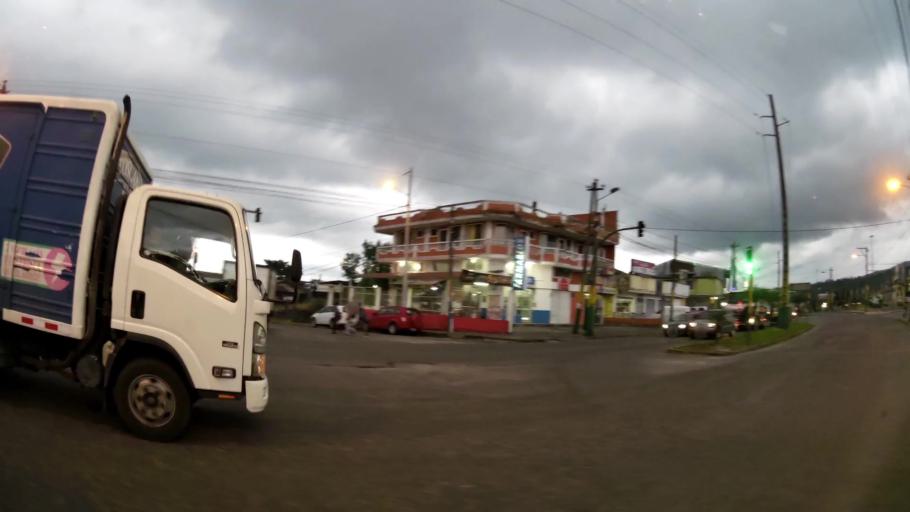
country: EC
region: Pastaza
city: Puyo
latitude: -1.4901
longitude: -78.0072
